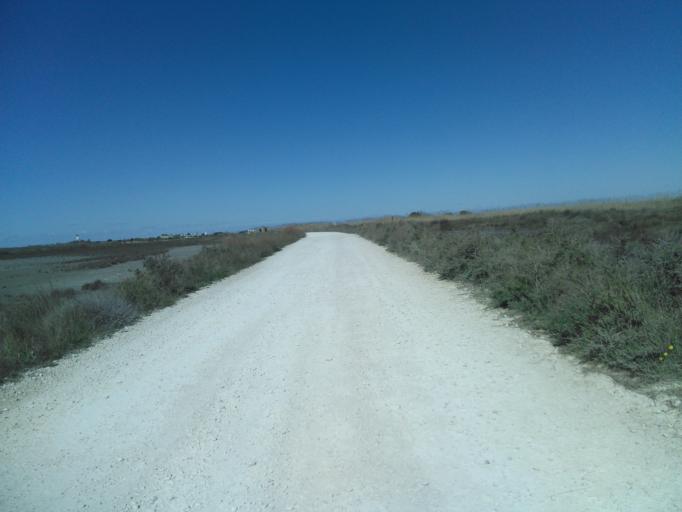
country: FR
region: Provence-Alpes-Cote d'Azur
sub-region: Departement des Bouches-du-Rhone
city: Saintes-Maries-de-la-Mer
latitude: 43.4535
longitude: 4.5867
